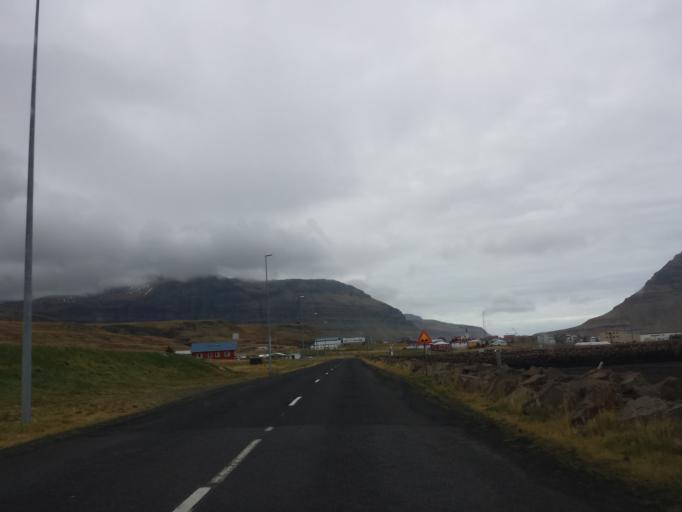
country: IS
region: West
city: Olafsvik
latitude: 64.9212
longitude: -23.2419
